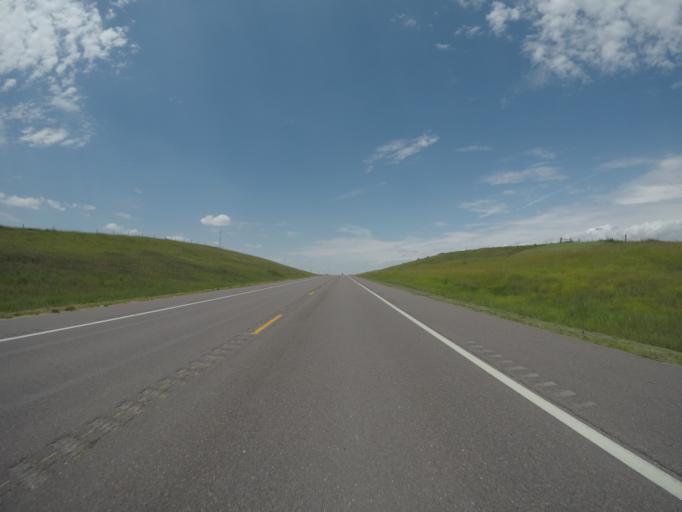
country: US
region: Kansas
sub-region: Graham County
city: Hill City
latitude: 39.3795
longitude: -99.7022
